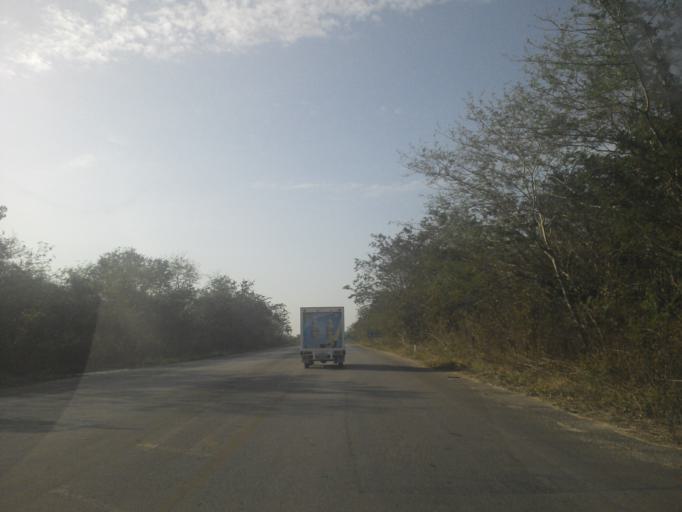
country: MX
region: Yucatan
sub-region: Valladolid
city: Tesoco
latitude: 20.7032
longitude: -88.1593
